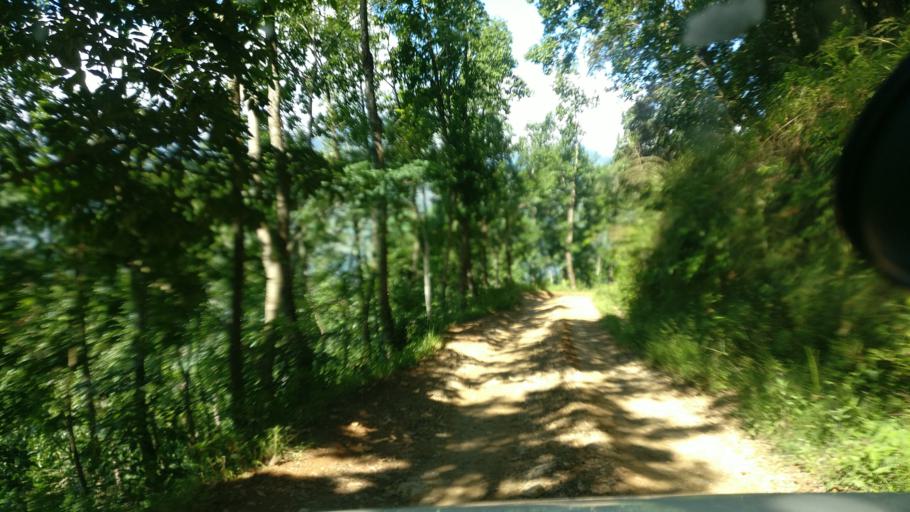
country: NP
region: Western Region
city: Baglung
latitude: 28.1360
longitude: 83.6548
